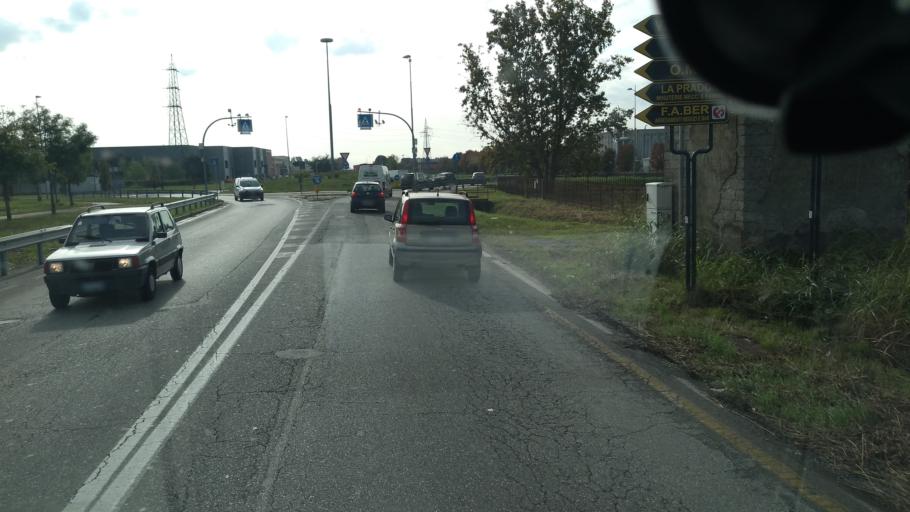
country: IT
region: Lombardy
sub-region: Provincia di Bergamo
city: Urgnano
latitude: 45.6198
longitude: 9.6914
